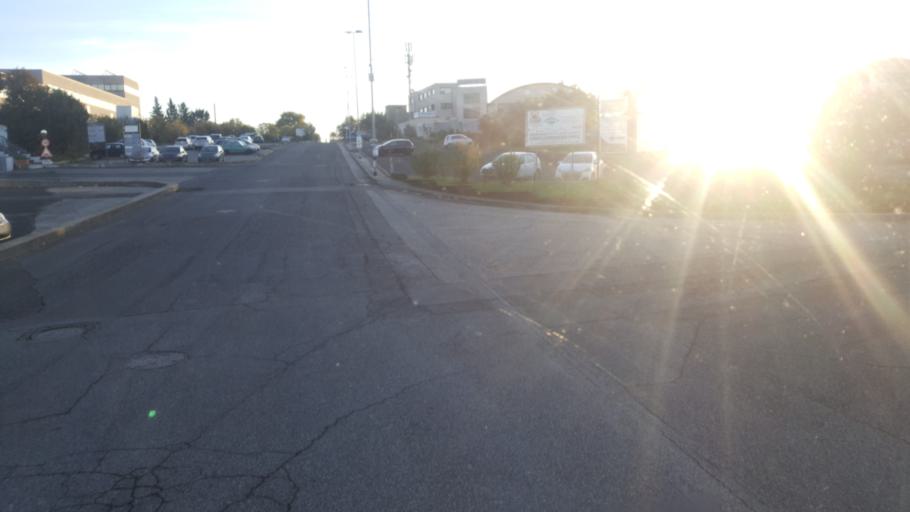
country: IT
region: Latium
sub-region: Citta metropolitana di Roma Capitale
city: Formello
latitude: 42.0531
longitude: 12.4020
